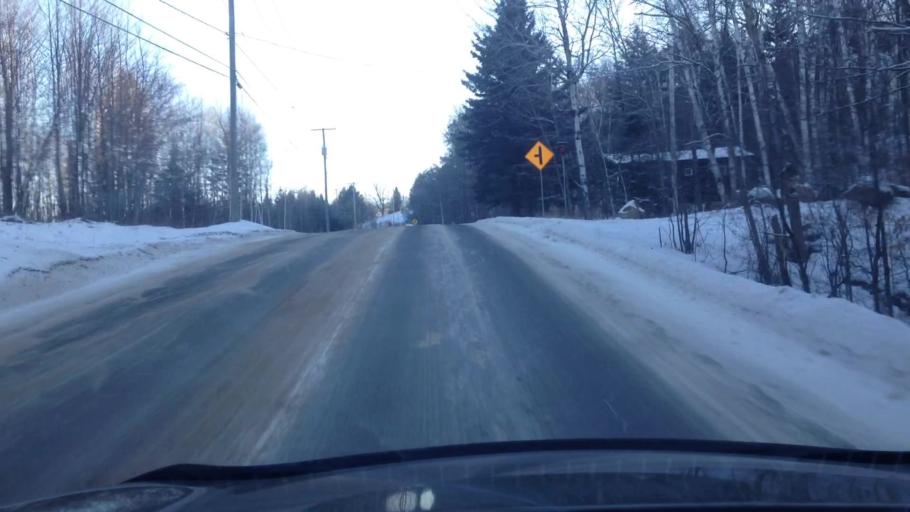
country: CA
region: Quebec
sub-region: Laurentides
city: Brownsburg-Chatham
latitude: 45.9220
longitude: -74.5032
